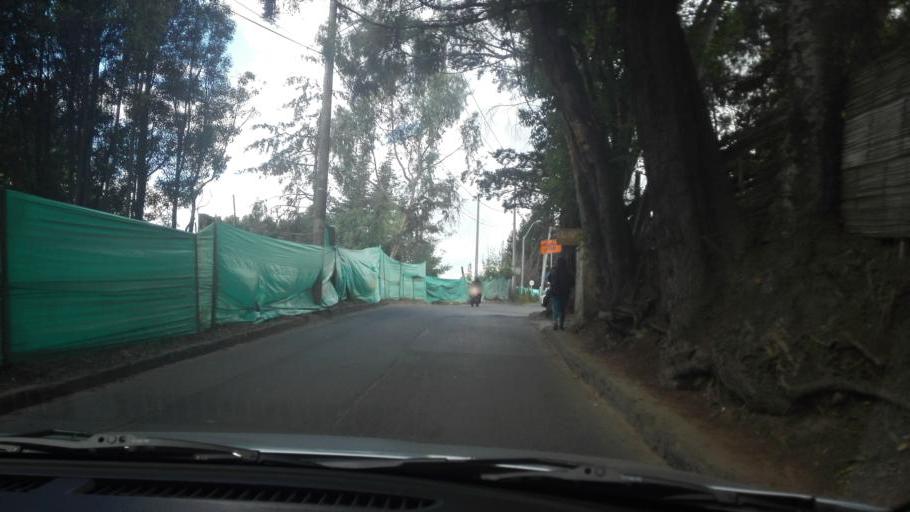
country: CO
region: Cundinamarca
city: Cota
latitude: 4.7404
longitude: -74.0732
